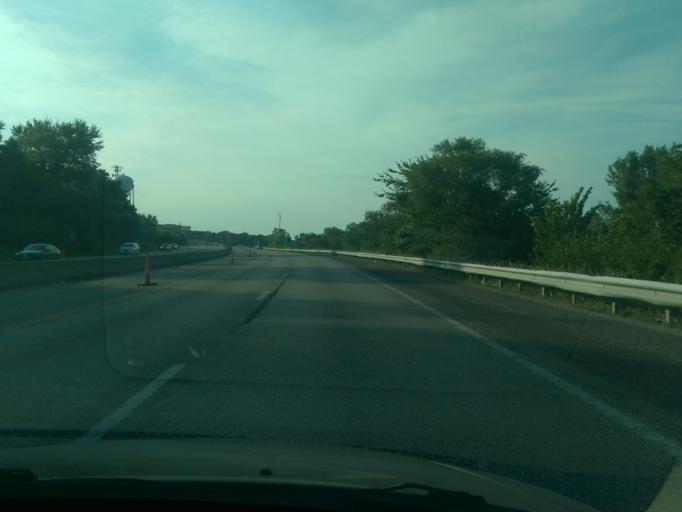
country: US
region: Missouri
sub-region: Platte County
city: Weatherby Lake
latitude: 39.2296
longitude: -94.6524
